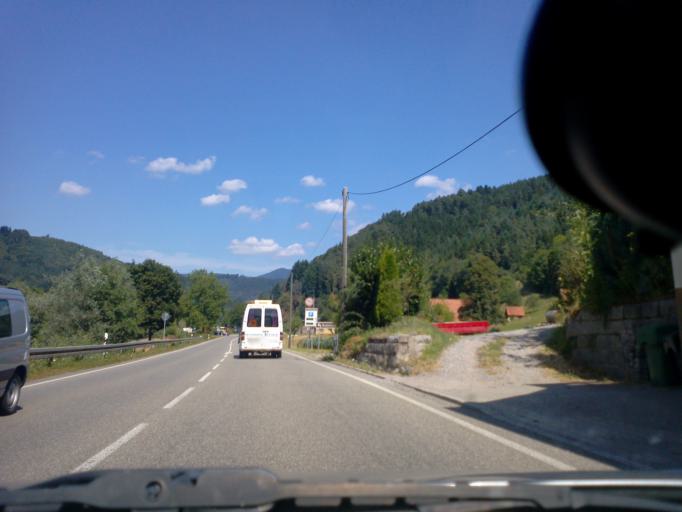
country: DE
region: Baden-Wuerttemberg
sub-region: Freiburg Region
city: Gutach (Schwarzwaldbahn)
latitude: 48.2672
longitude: 8.2041
